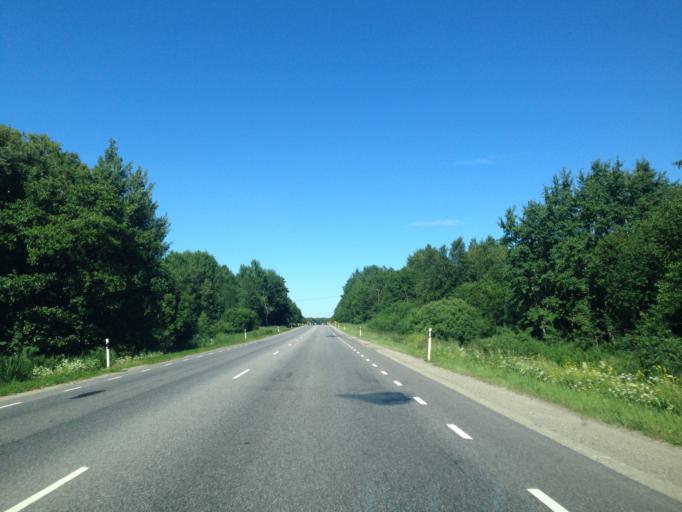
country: EE
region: Harju
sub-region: Rae vald
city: Jueri
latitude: 59.3655
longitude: 24.9029
